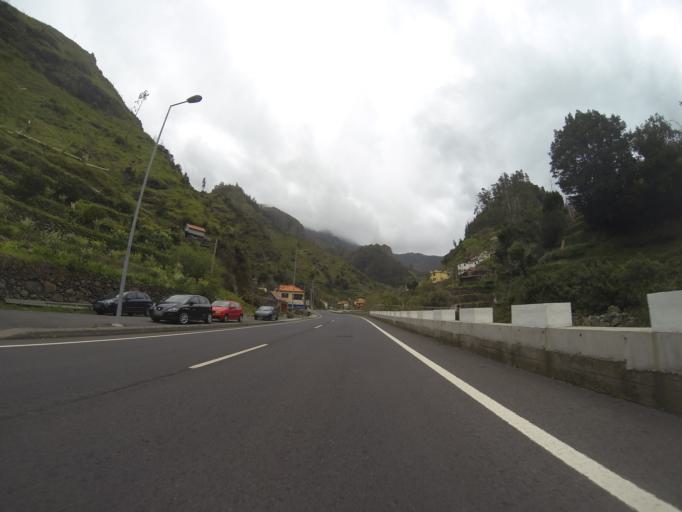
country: PT
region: Madeira
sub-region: Camara de Lobos
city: Curral das Freiras
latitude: 32.7330
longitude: -17.0209
